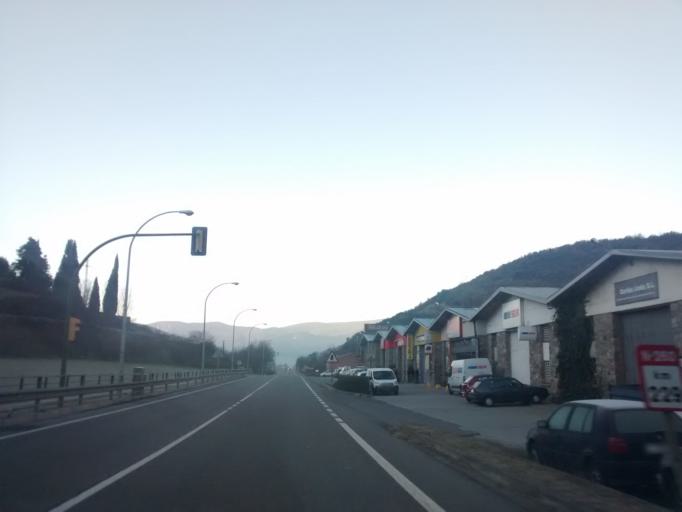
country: ES
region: Catalonia
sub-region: Provincia de Lleida
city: la Seu d'Urgell
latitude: 42.3560
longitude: 1.4425
